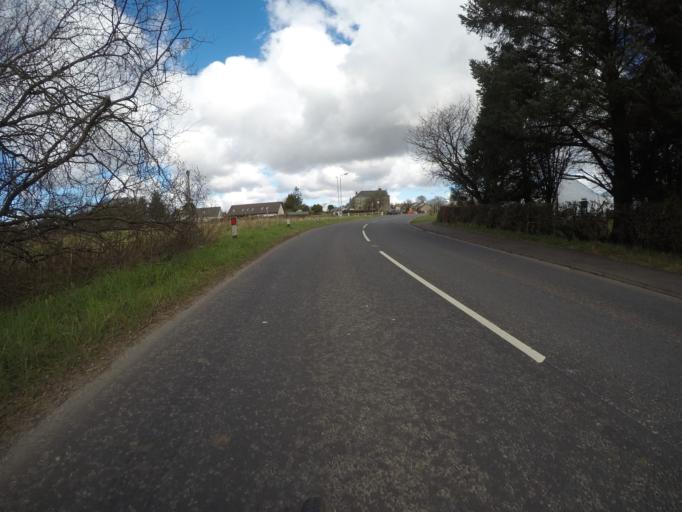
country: GB
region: Scotland
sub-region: North Ayrshire
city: Beith
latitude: 55.7456
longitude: -4.6292
